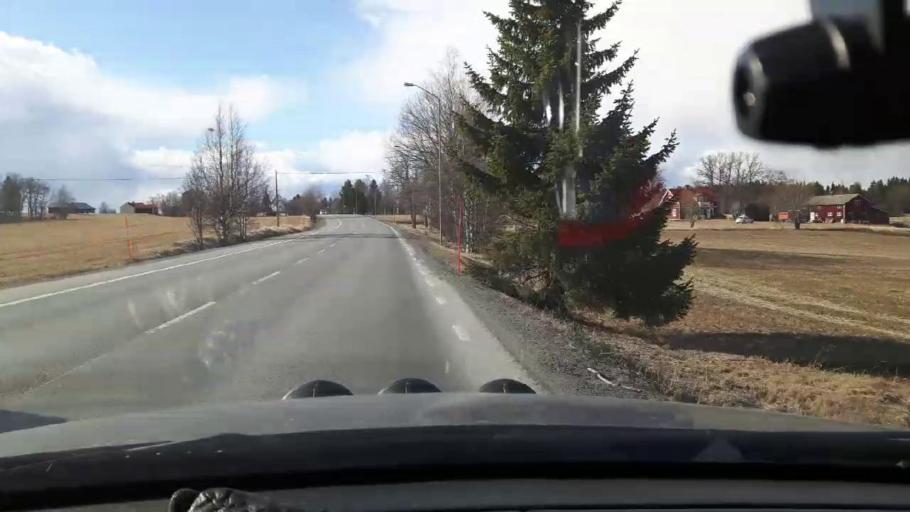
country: SE
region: Jaemtland
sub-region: OEstersunds Kommun
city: Ostersund
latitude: 63.1753
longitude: 14.5317
